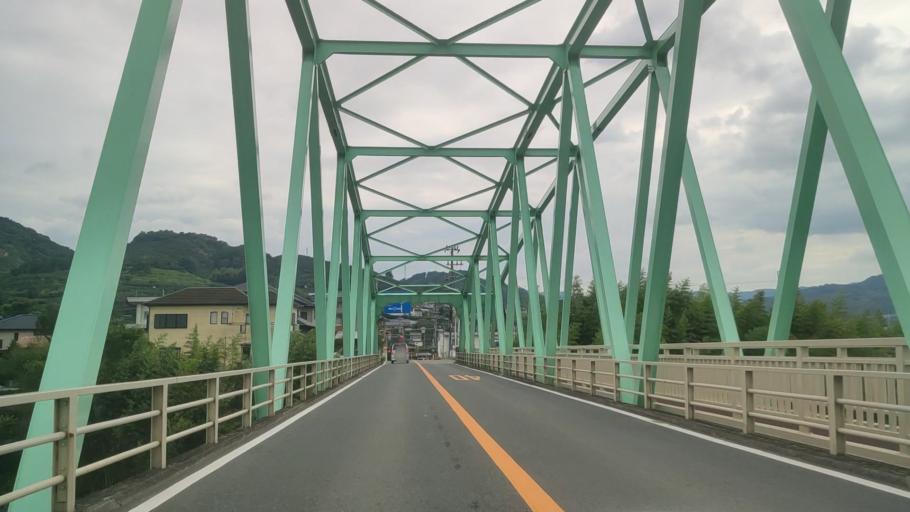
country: JP
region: Wakayama
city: Hashimoto
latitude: 34.2985
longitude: 135.5782
